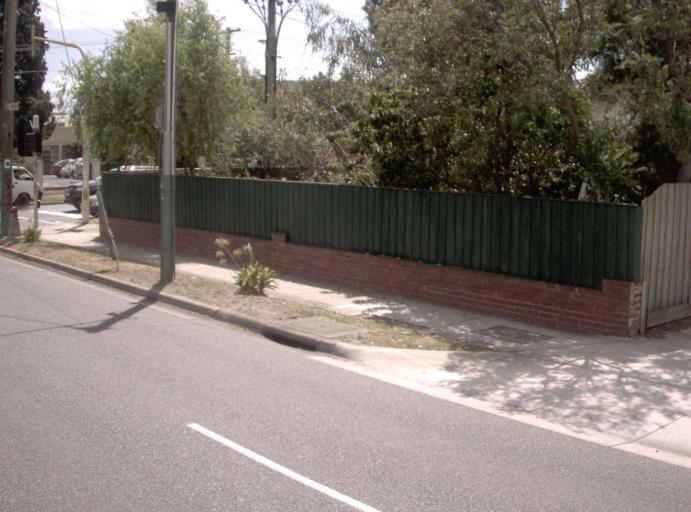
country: AU
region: Victoria
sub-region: Monash
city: Ashwood
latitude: -37.8536
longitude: 145.0951
